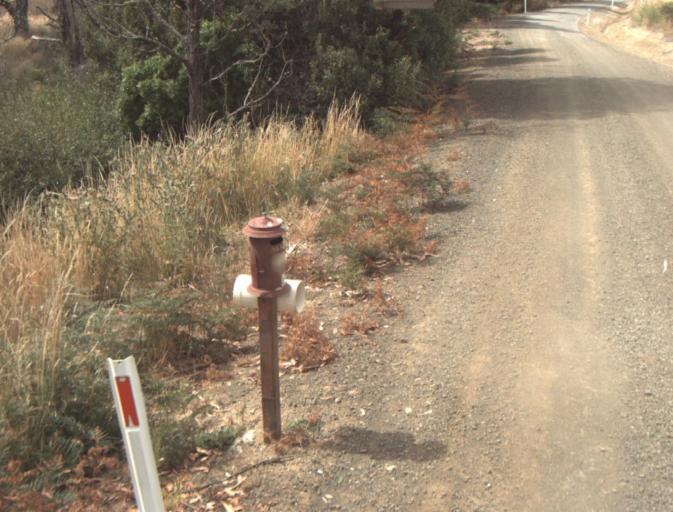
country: AU
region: Tasmania
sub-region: Northern Midlands
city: Evandale
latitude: -41.4600
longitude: 147.4477
